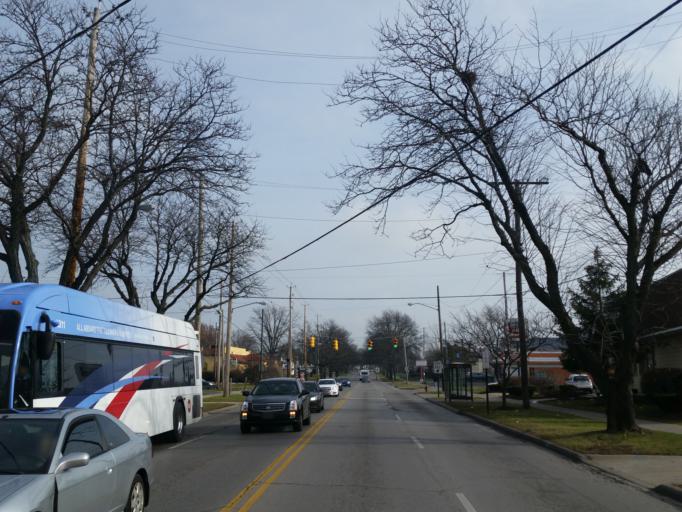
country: US
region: Ohio
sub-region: Cuyahoga County
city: Maple Heights
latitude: 41.4493
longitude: -81.5798
